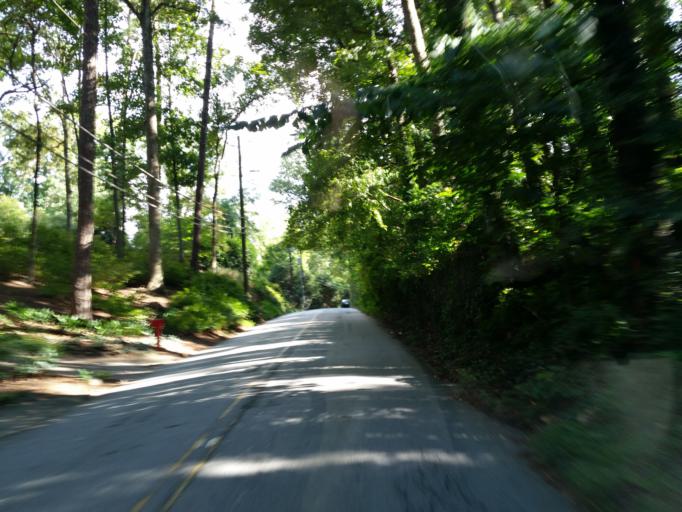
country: US
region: Georgia
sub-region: Cobb County
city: Vinings
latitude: 33.8569
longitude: -84.4385
